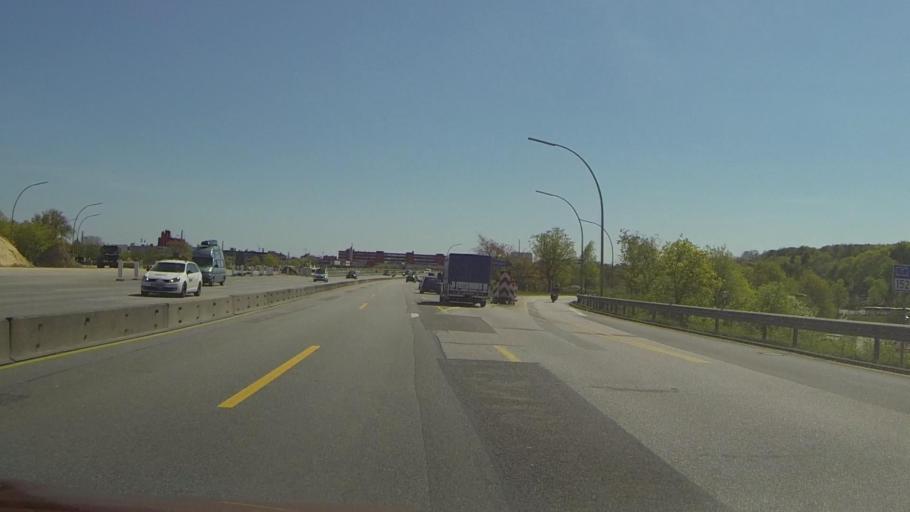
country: DE
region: Hamburg
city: Stellingen
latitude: 53.5860
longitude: 9.9155
